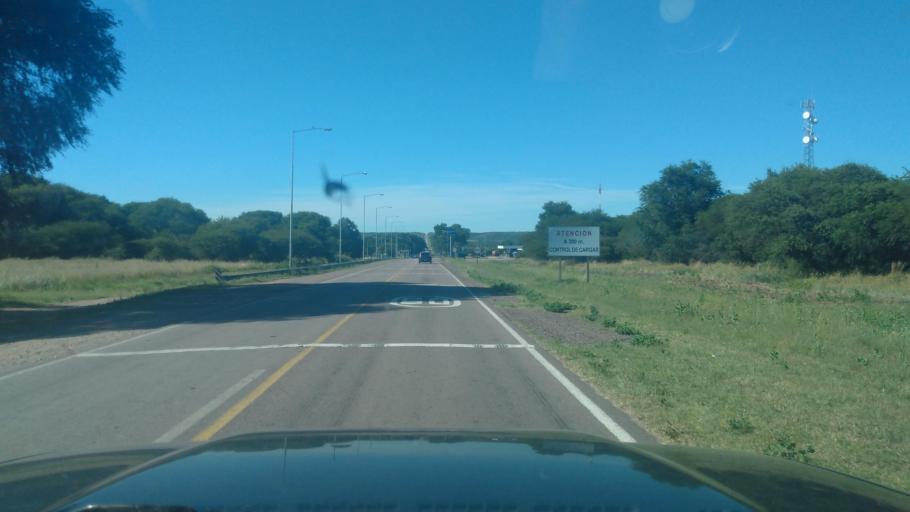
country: AR
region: La Pampa
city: Doblas
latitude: -37.3036
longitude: -64.2879
